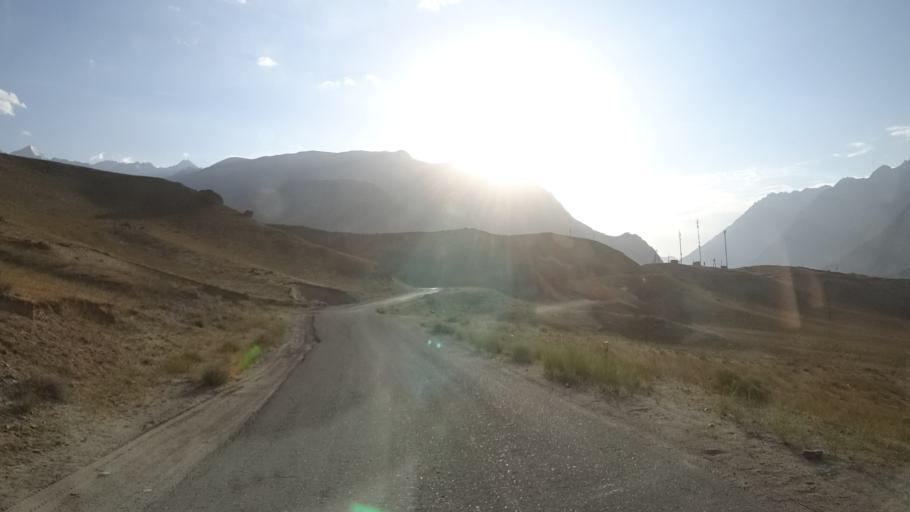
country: TJ
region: Gorno-Badakhshan
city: Vanj
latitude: 38.2912
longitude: 71.3415
